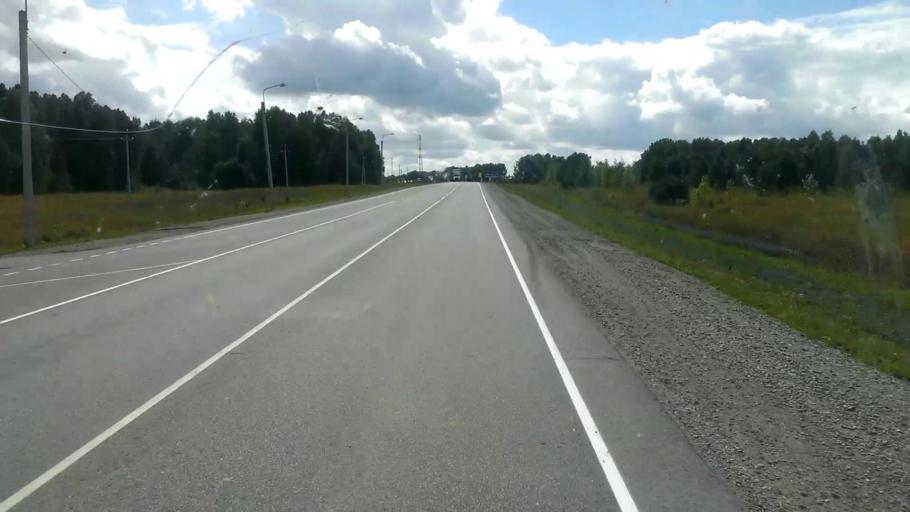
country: RU
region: Altai Krai
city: Troitskoye
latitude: 52.9738
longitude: 84.7473
